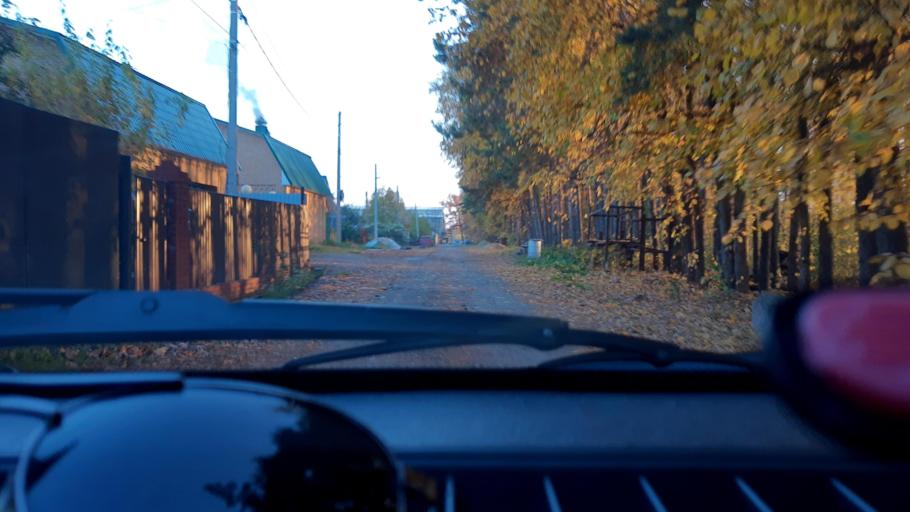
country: RU
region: Bashkortostan
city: Ufa
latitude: 54.7847
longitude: 55.9459
